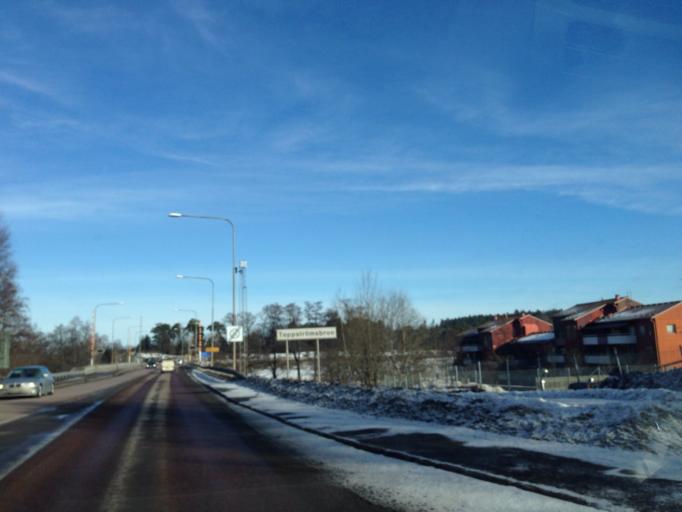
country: SE
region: Stockholm
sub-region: Ekero Kommun
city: Ekeroe
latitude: 59.2916
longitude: 17.8094
